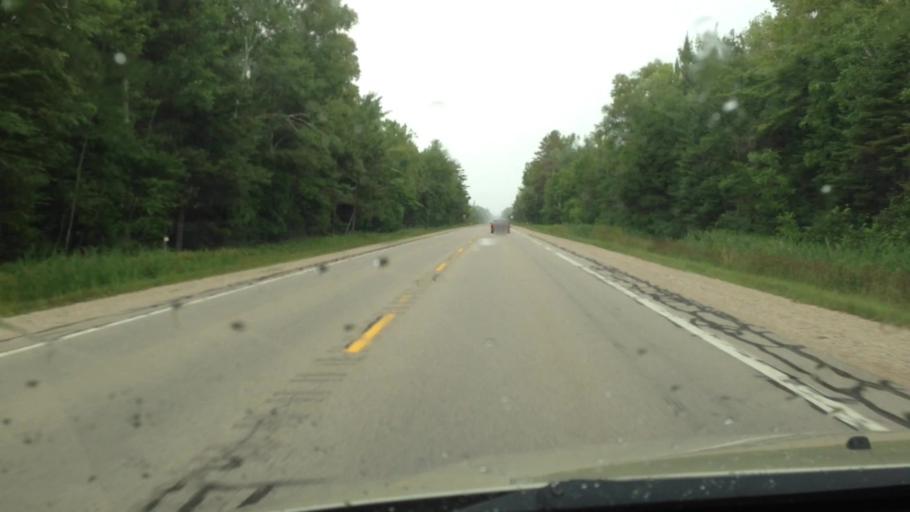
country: US
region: Michigan
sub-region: Menominee County
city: Menominee
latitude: 45.3856
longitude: -87.3735
